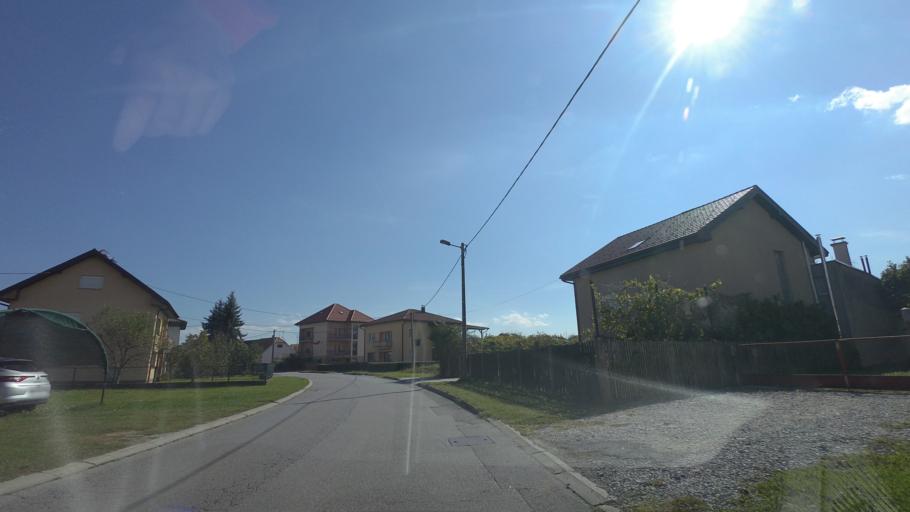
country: HR
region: Karlovacka
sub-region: Grad Karlovac
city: Karlovac
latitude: 45.4975
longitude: 15.5394
